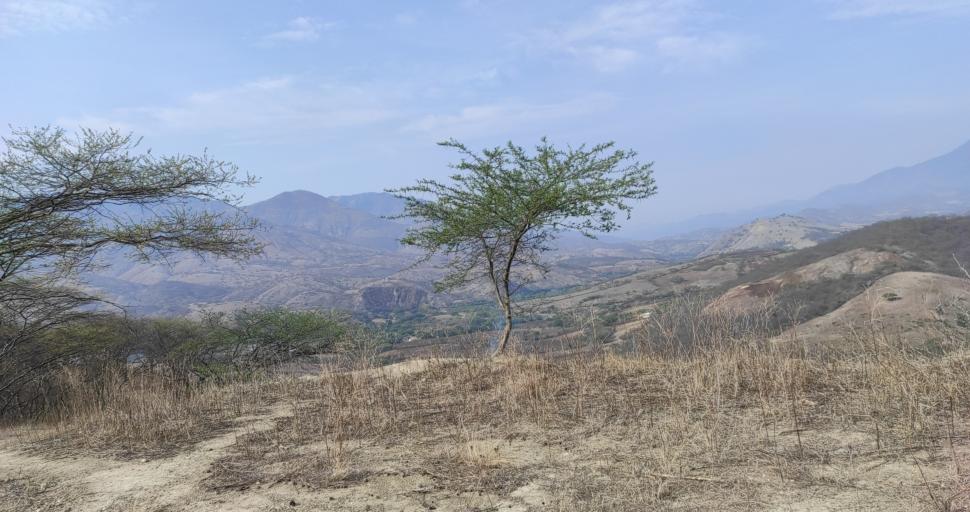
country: EC
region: Loja
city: Catacocha
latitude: -4.0191
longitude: -79.7049
